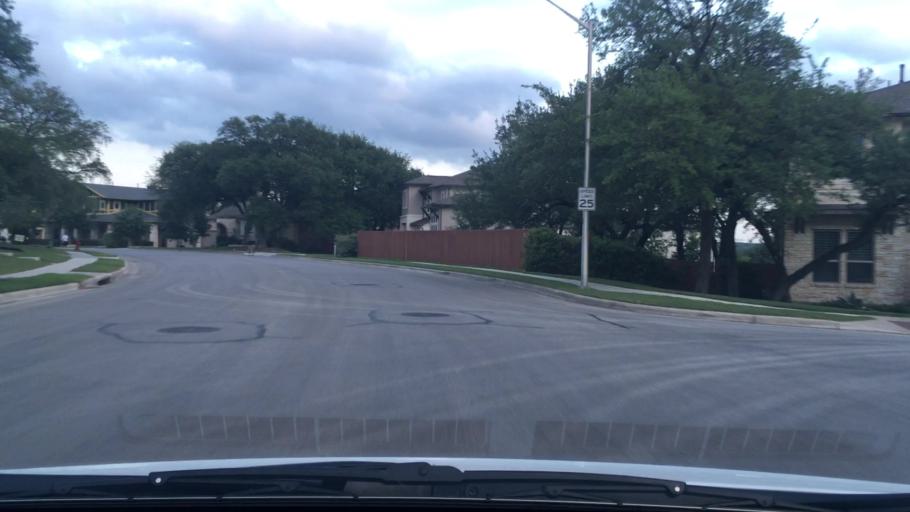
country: US
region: Texas
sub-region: Williamson County
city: Anderson Mill
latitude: 30.4540
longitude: -97.8581
